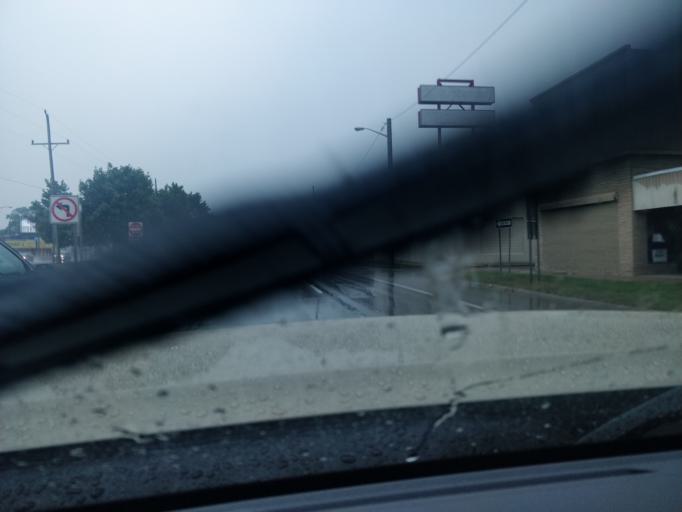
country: US
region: Michigan
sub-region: Wayne County
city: Lincoln Park
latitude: 42.2307
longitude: -83.1808
